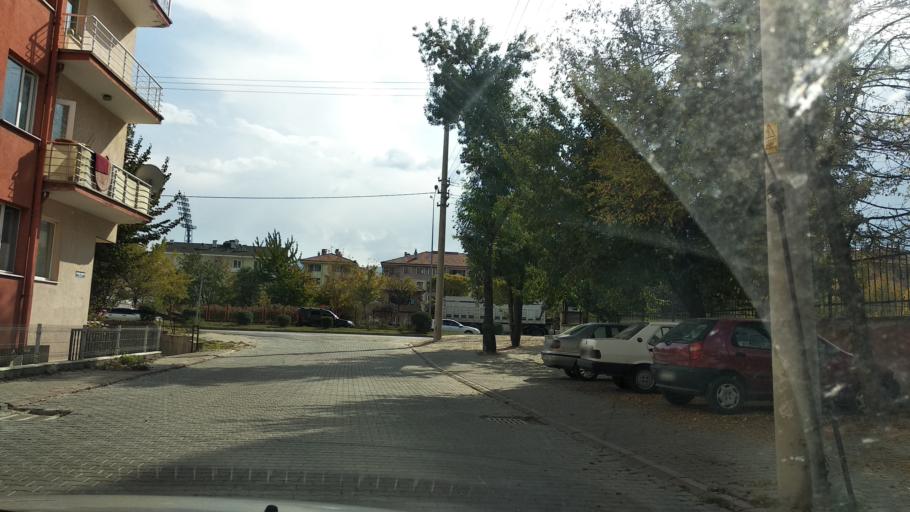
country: TR
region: Bolu
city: Bolu
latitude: 40.7389
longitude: 31.6044
